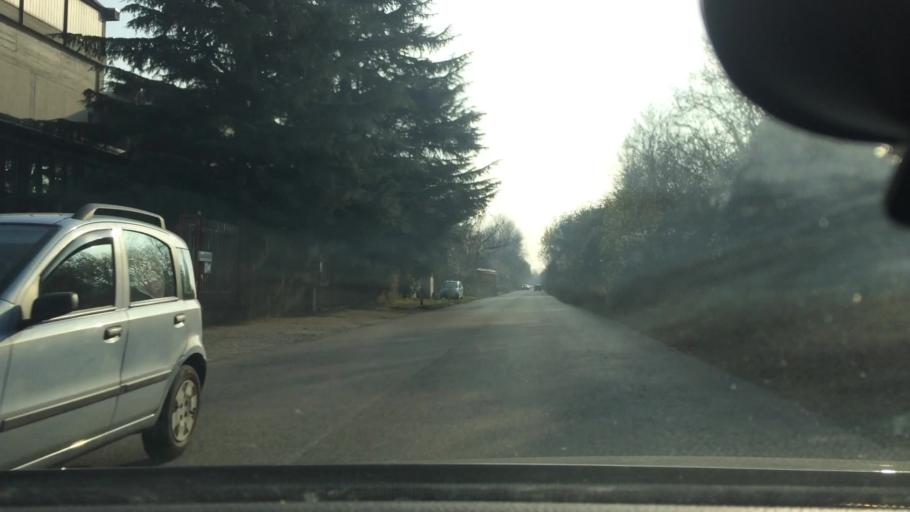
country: IT
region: Lombardy
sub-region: Provincia di Monza e Brianza
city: Villaggio del Sole
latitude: 45.6045
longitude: 9.0954
